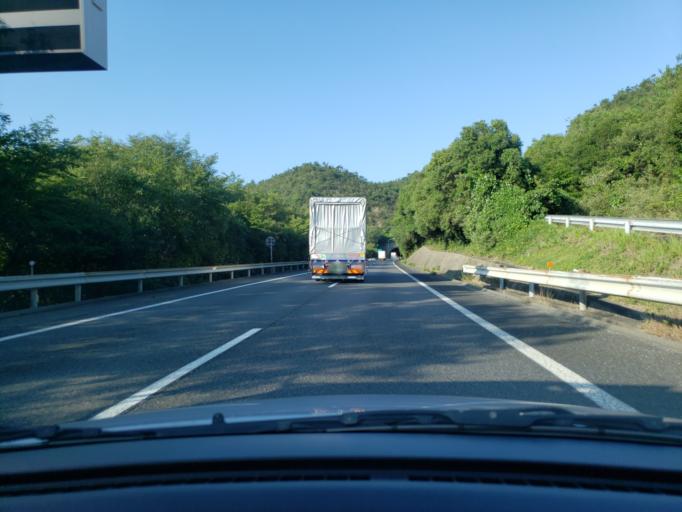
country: JP
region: Okayama
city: Kurashiki
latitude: 34.6149
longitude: 133.7386
